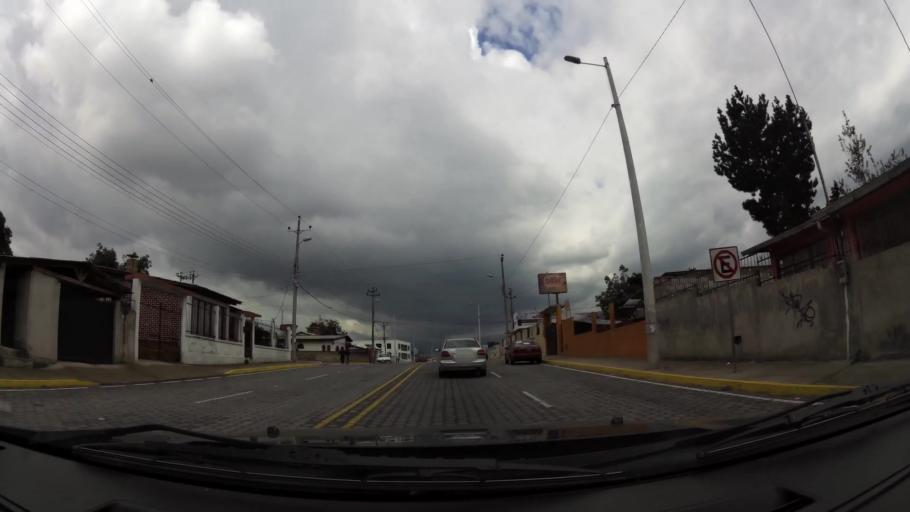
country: EC
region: Pichincha
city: Sangolqui
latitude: -0.3298
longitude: -78.4543
